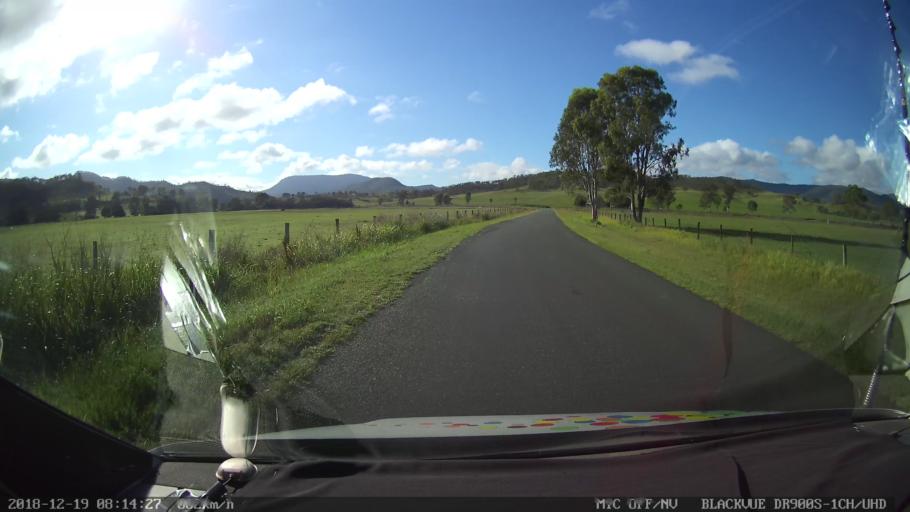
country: AU
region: Queensland
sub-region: Logan
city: Cedar Vale
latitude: -28.2473
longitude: 152.8913
